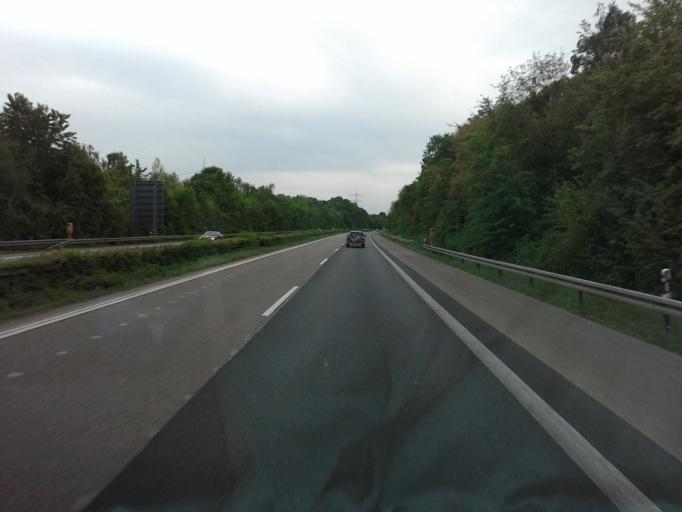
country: DE
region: North Rhine-Westphalia
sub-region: Regierungsbezirk Koln
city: Erftstadt
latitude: 50.8436
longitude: 6.8008
